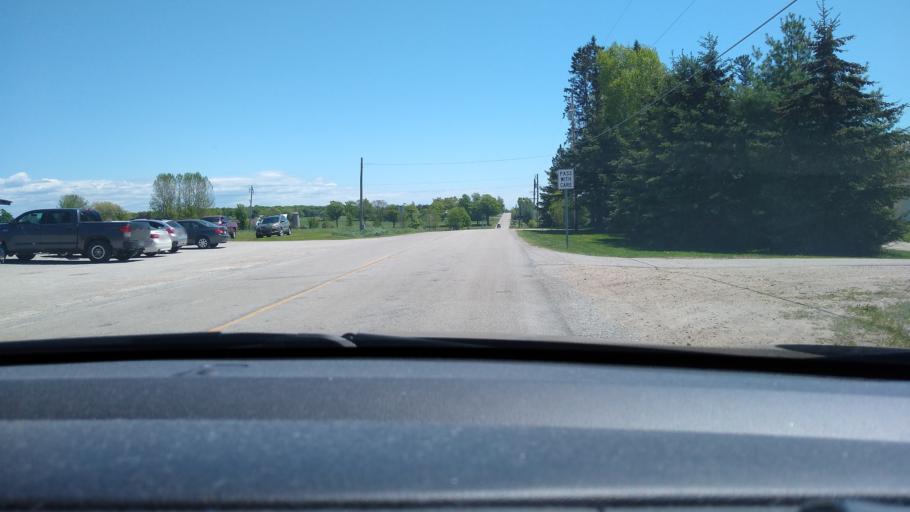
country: US
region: Michigan
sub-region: Delta County
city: Escanaba
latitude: 45.8261
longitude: -87.1439
